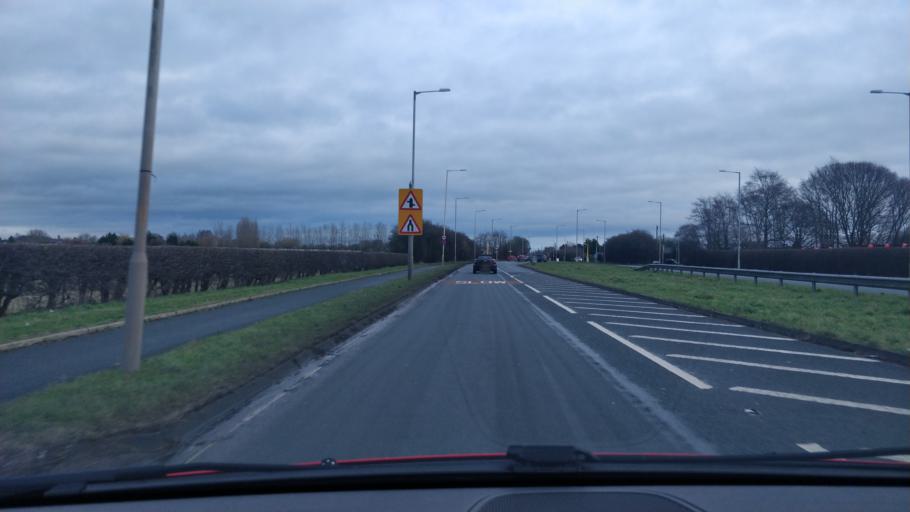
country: GB
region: England
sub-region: Lancashire
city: Tarleton
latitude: 53.6677
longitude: -2.8585
